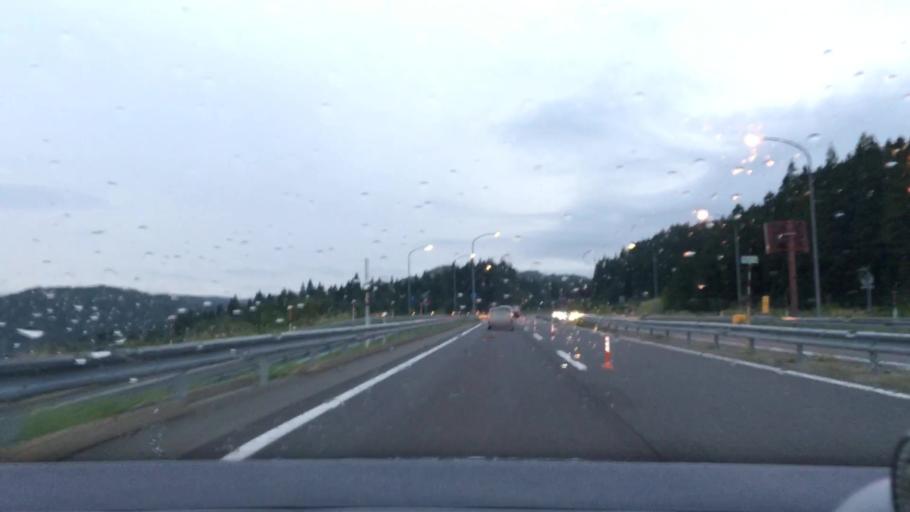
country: JP
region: Gifu
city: Gujo
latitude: 35.9374
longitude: 136.8811
